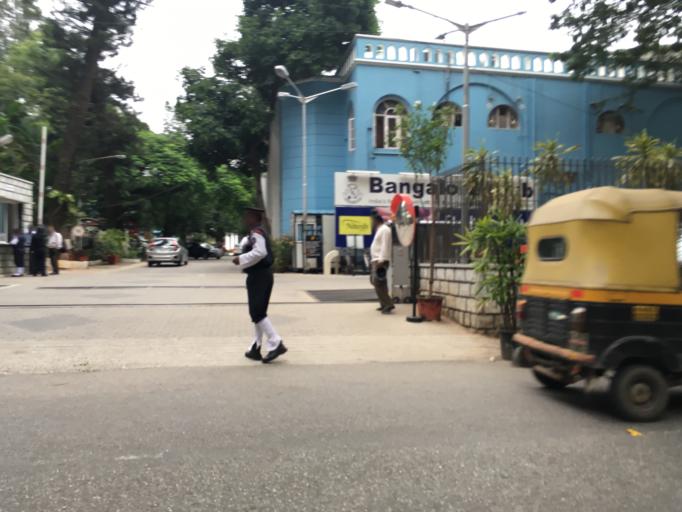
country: IN
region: Karnataka
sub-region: Bangalore Urban
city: Bangalore
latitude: 12.9670
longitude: 77.5965
